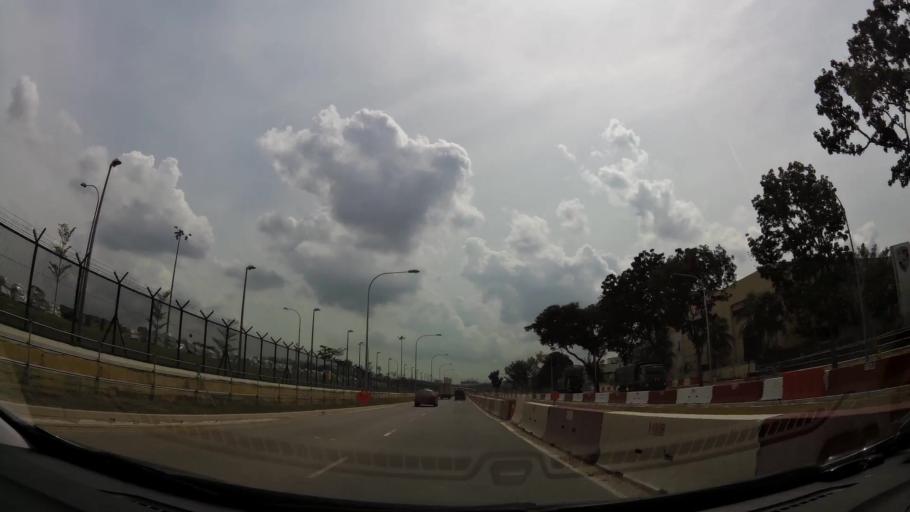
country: MY
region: Johor
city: Johor Bahru
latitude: 1.4023
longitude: 103.7561
